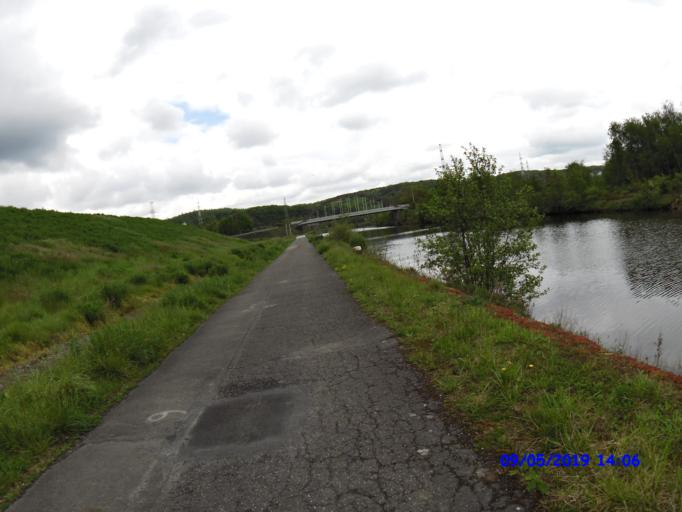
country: BE
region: Wallonia
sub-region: Province du Hainaut
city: Farciennes
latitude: 50.4388
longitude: 4.5572
